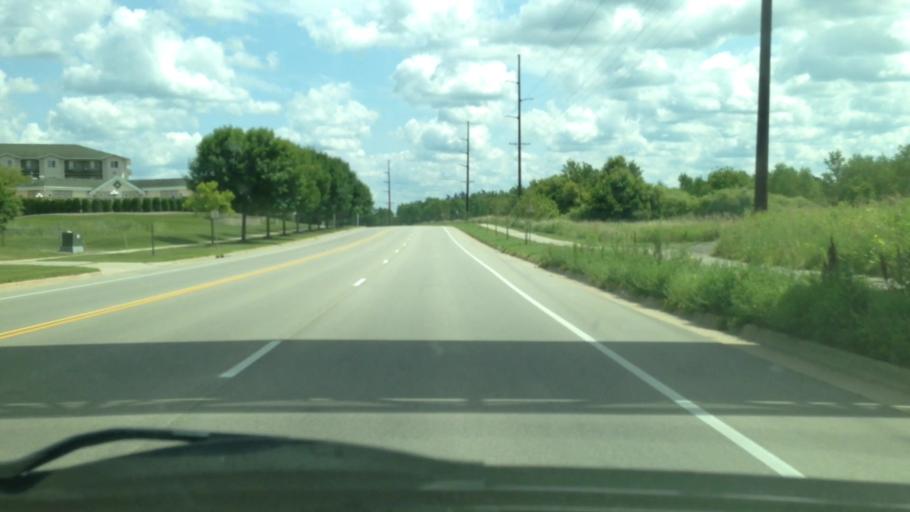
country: US
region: Minnesota
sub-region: Olmsted County
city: Rochester
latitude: 44.0635
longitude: -92.5200
